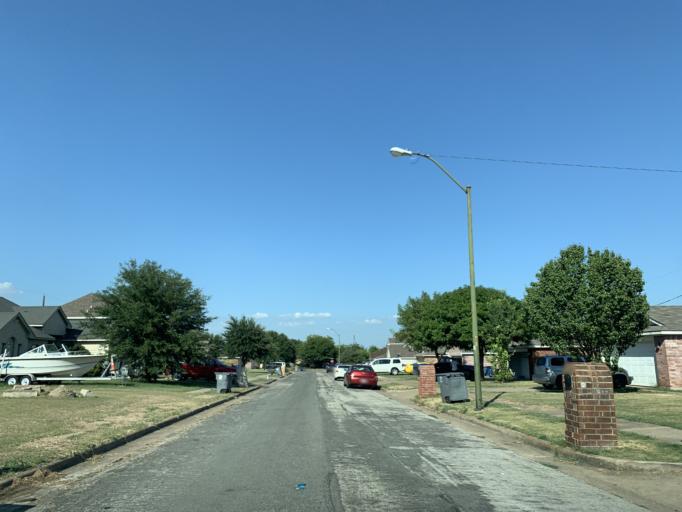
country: US
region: Texas
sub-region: Dallas County
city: Hutchins
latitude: 32.6585
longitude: -96.7729
